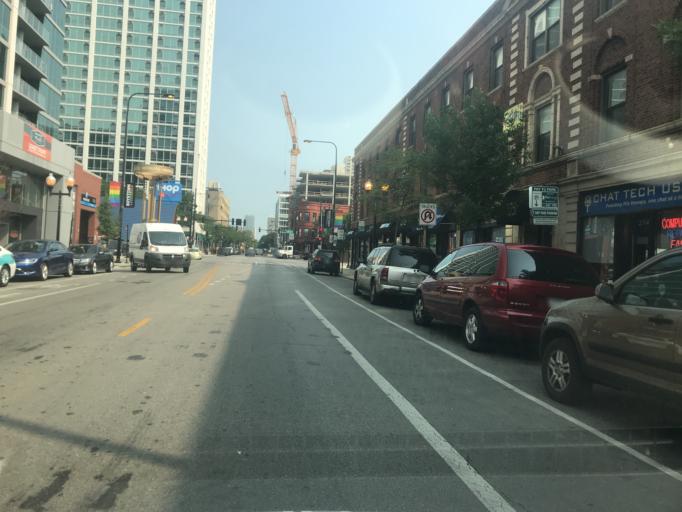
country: US
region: Illinois
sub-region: Cook County
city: Lincolnwood
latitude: 41.9501
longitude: -87.6495
